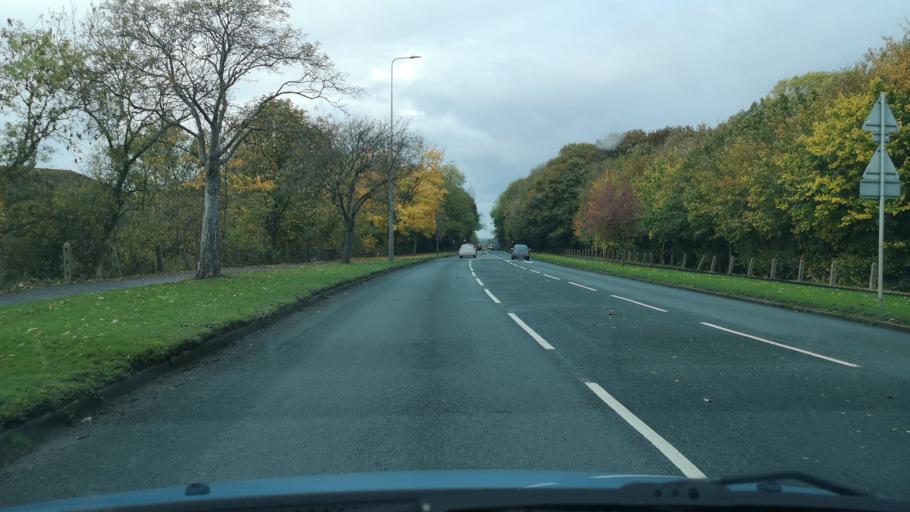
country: GB
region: England
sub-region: North Lincolnshire
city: Scunthorpe
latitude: 53.5811
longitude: -0.6693
